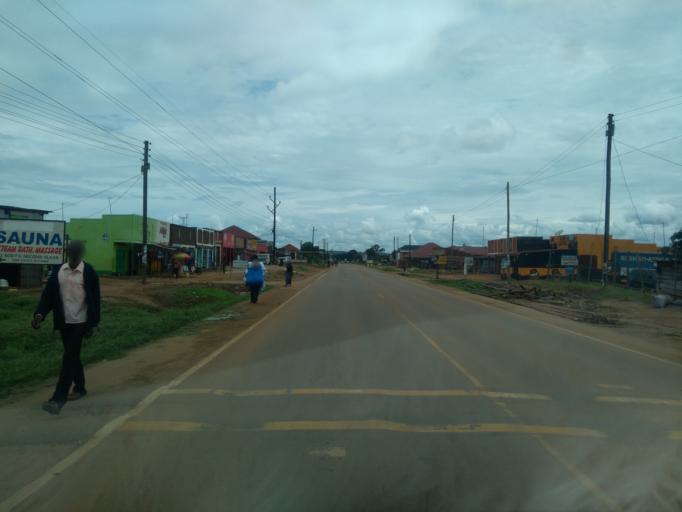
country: UG
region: Central Region
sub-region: Butambala District
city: Gombe
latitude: -0.0145
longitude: 32.0299
